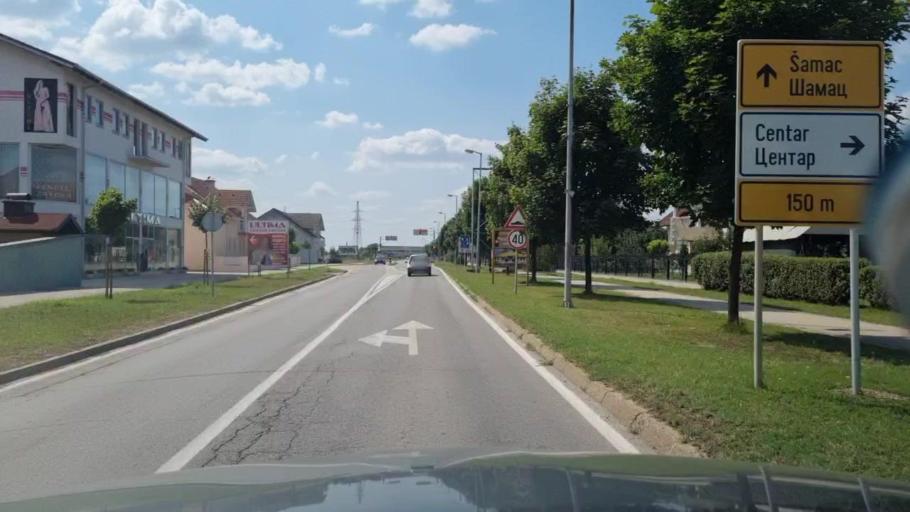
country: BA
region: Federation of Bosnia and Herzegovina
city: Orasje
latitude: 45.0274
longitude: 18.6941
